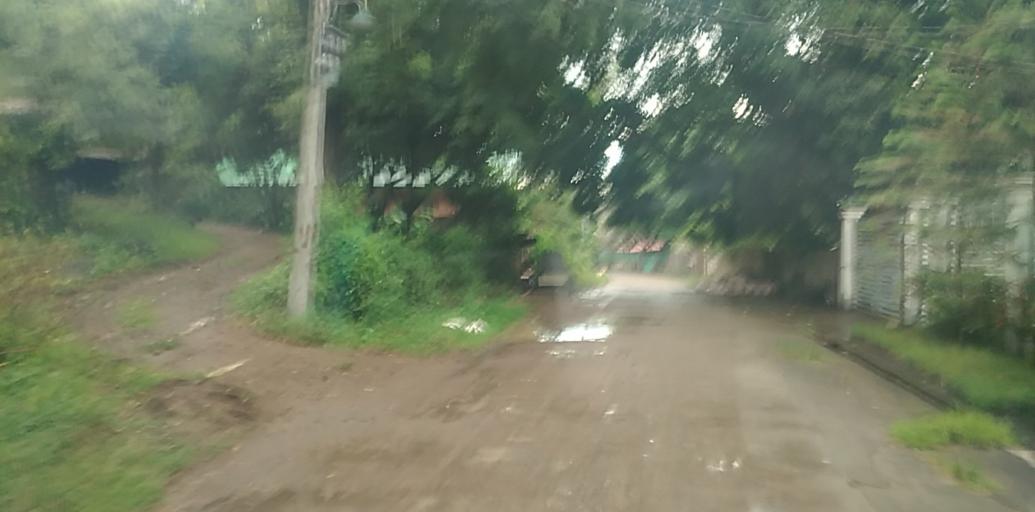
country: PH
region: Central Luzon
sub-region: Province of Pampanga
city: Arayat
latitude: 15.1528
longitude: 120.7445
